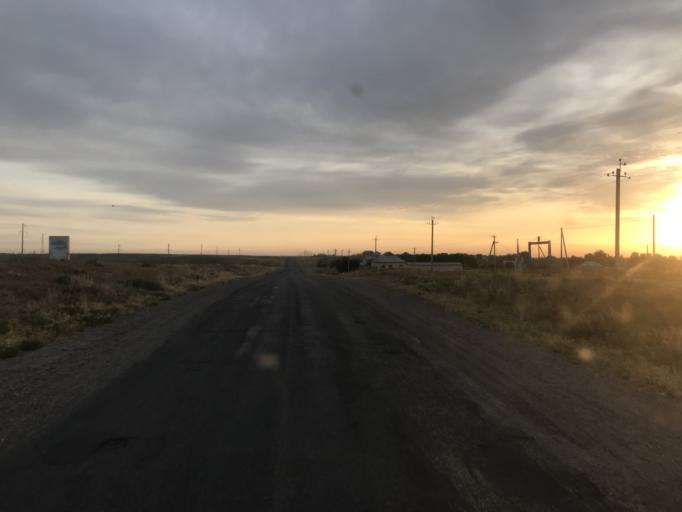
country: UZ
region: Toshkent
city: Amir Timur
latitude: 41.2312
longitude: 68.8087
